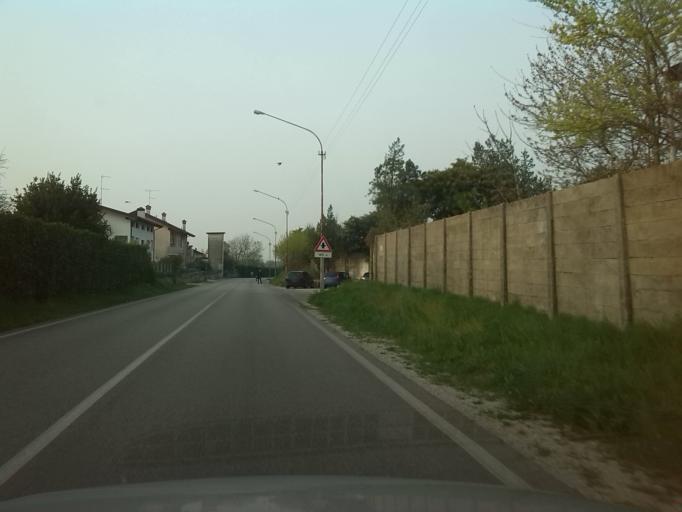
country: IT
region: Friuli Venezia Giulia
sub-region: Provincia di Udine
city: Cividale del Friuli
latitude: 46.0877
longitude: 13.4168
